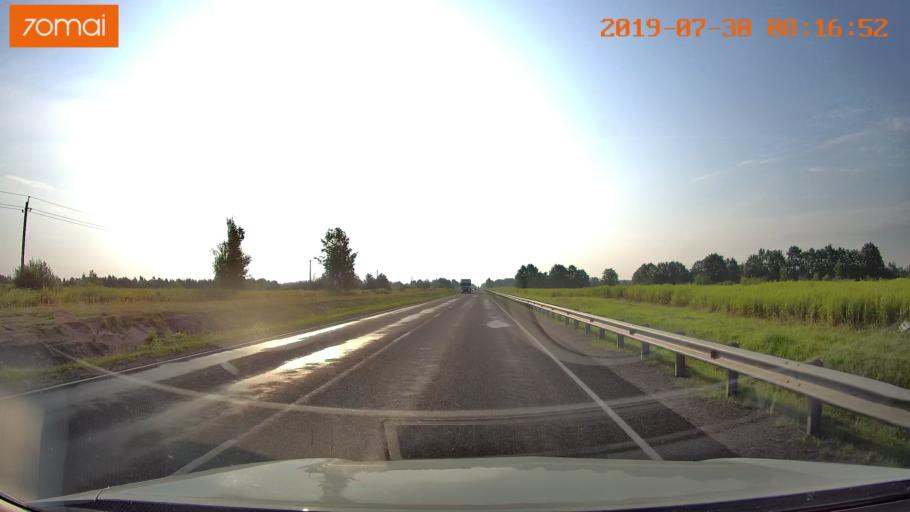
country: RU
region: Kaliningrad
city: Zheleznodorozhnyy
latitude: 54.6386
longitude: 21.4220
